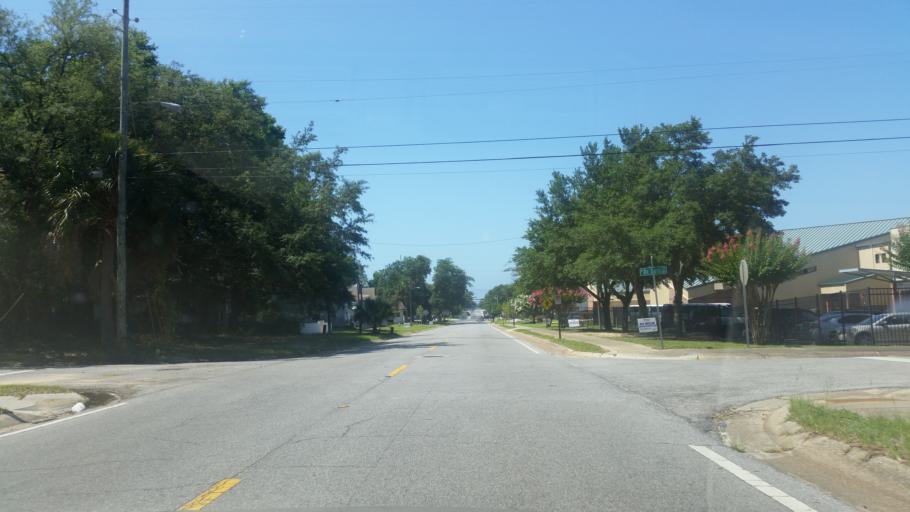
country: US
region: Florida
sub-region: Escambia County
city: Pensacola
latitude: 30.4222
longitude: -87.2255
